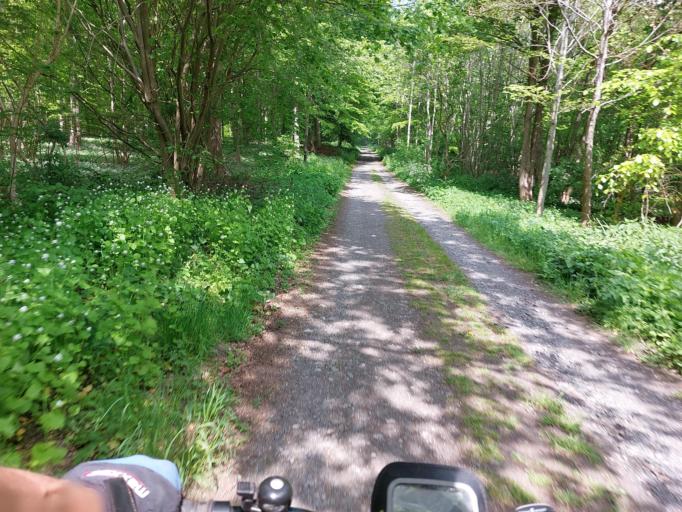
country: BE
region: Wallonia
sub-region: Province du Hainaut
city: Quaregnon
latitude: 50.4864
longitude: 3.8542
